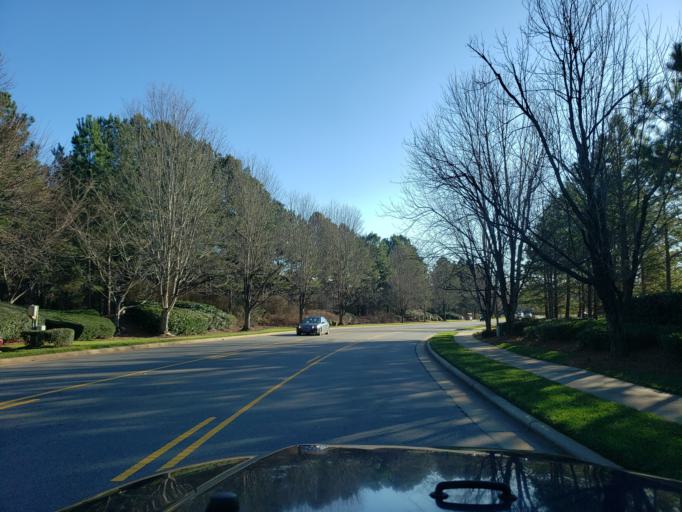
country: US
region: North Carolina
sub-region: Catawba County
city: Lake Norman of Catawba
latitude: 35.5392
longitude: -80.9170
